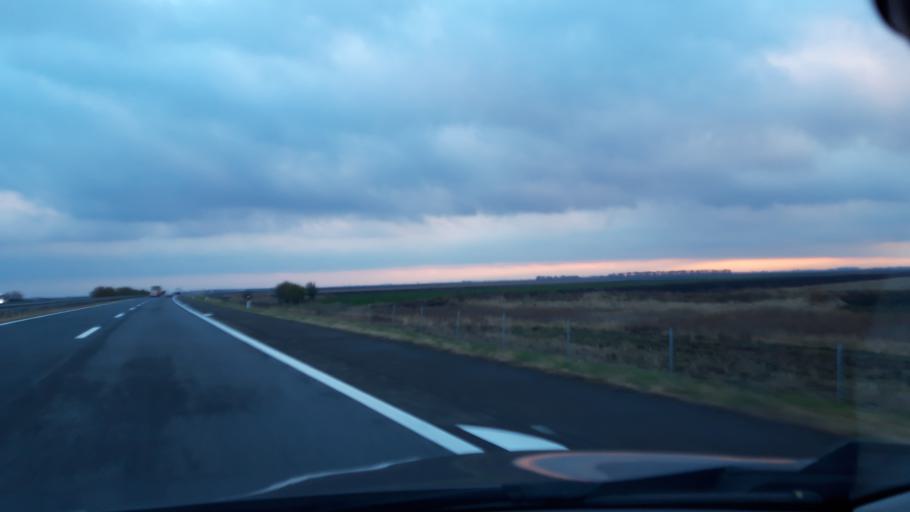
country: RS
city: Zmajevo
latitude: 45.5013
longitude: 19.7275
